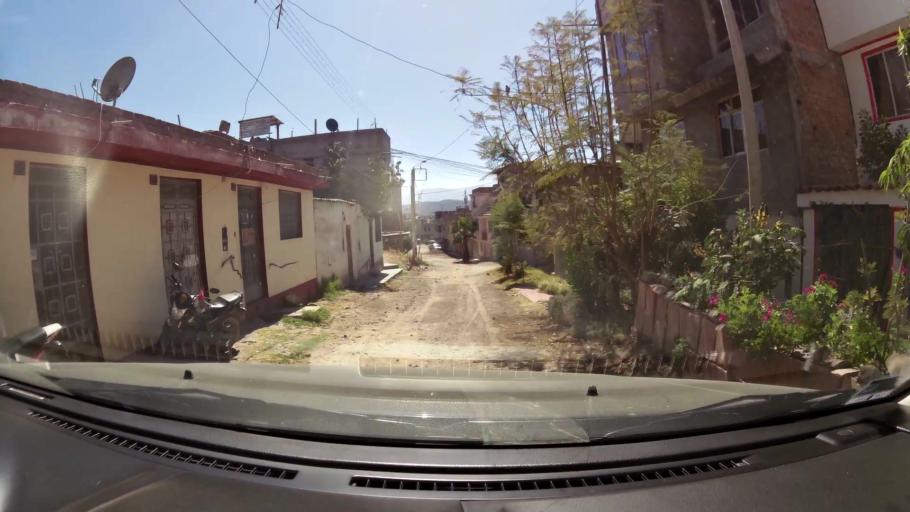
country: PE
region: Ayacucho
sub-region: Provincia de Huamanga
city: Ayacucho
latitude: -13.1529
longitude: -74.2313
